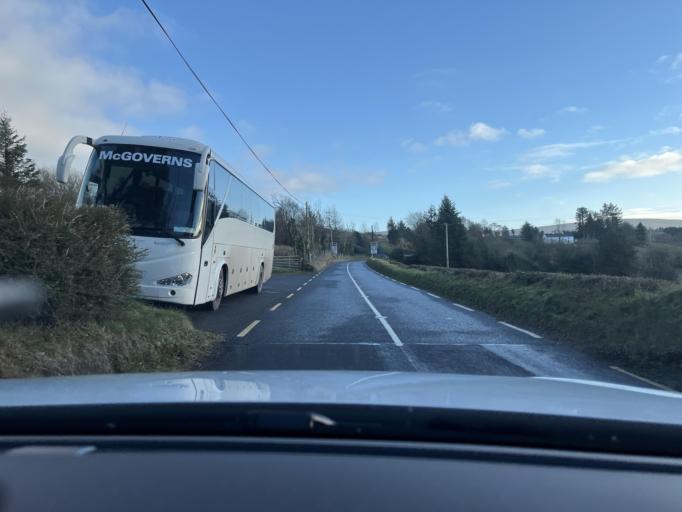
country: GB
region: Northern Ireland
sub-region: Fermanagh District
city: Enniskillen
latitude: 54.1910
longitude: -7.8875
